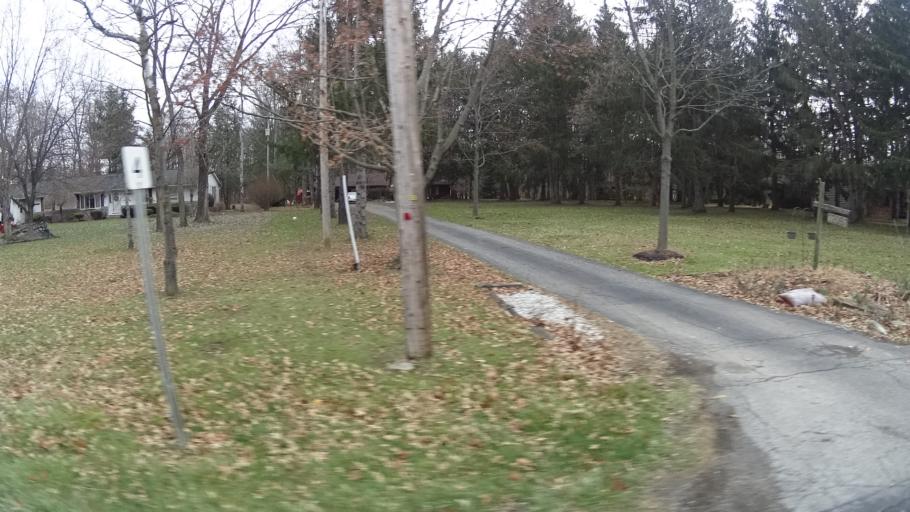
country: US
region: Ohio
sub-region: Cuyahoga County
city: Olmsted Falls
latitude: 41.3304
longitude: -81.9078
